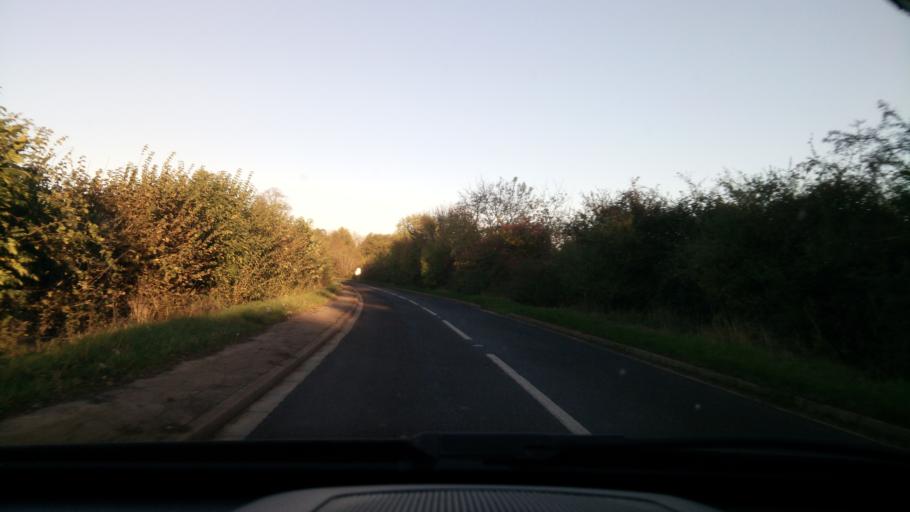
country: GB
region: England
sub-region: Peterborough
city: Ufford
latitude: 52.6379
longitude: -0.3928
